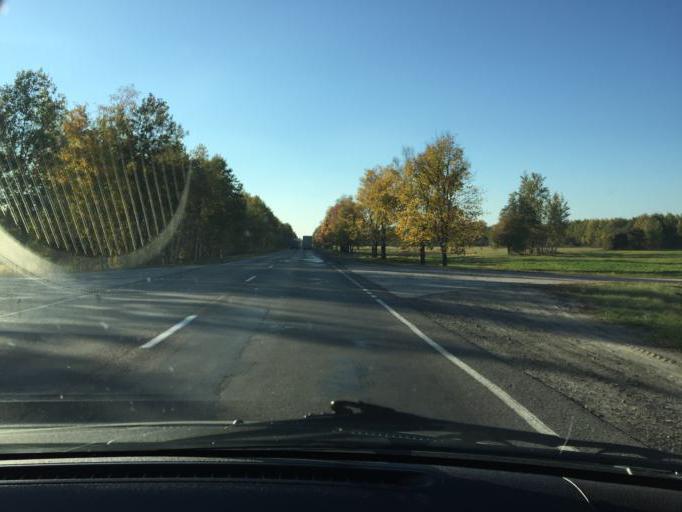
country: BY
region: Brest
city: Luninyets
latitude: 52.2744
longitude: 26.8952
